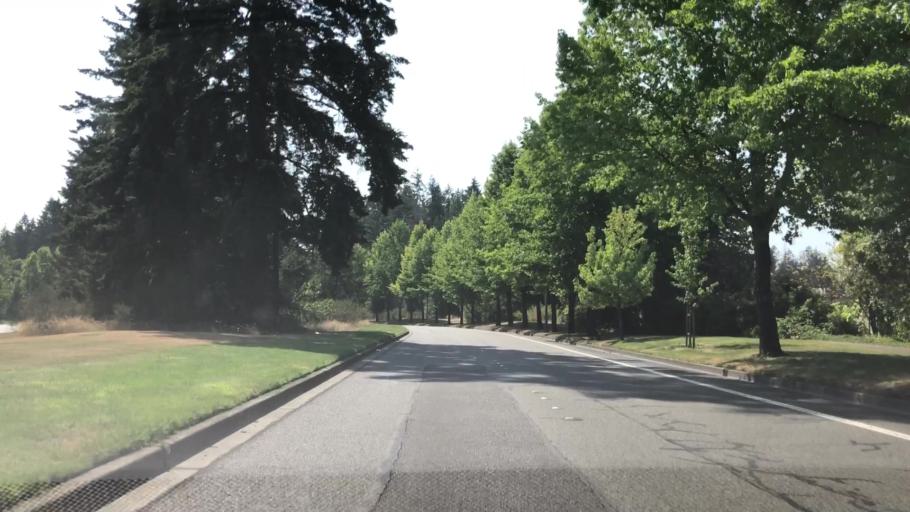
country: US
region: Washington
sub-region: Thurston County
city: Tanglewilde-Thompson Place
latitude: 47.0701
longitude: -122.7602
